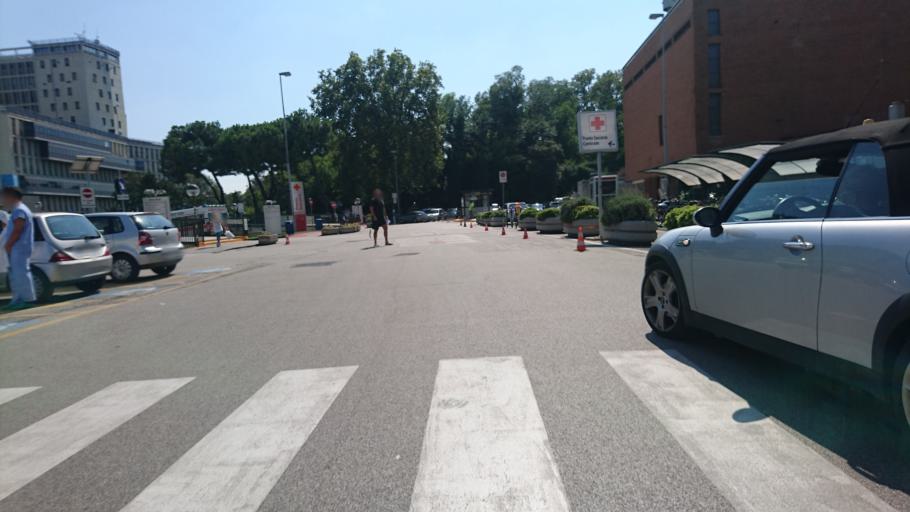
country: IT
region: Veneto
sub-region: Provincia di Padova
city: Padova
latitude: 45.4030
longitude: 11.8871
